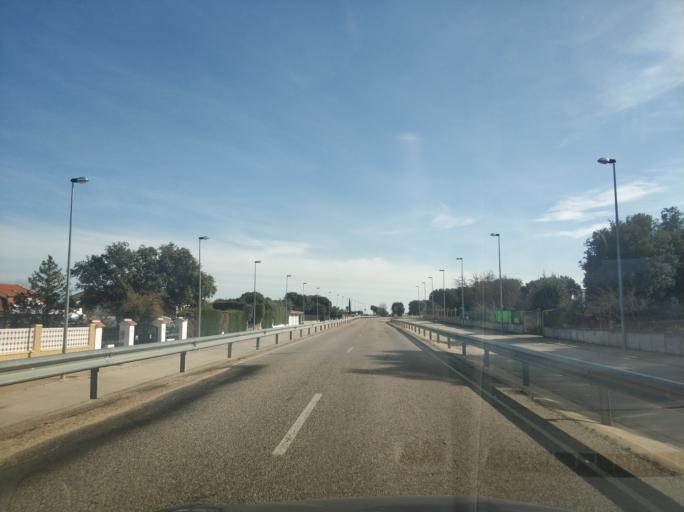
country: ES
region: Castille and Leon
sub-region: Provincia de Salamanca
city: Florida de Liebana
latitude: 41.0185
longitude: -5.7451
